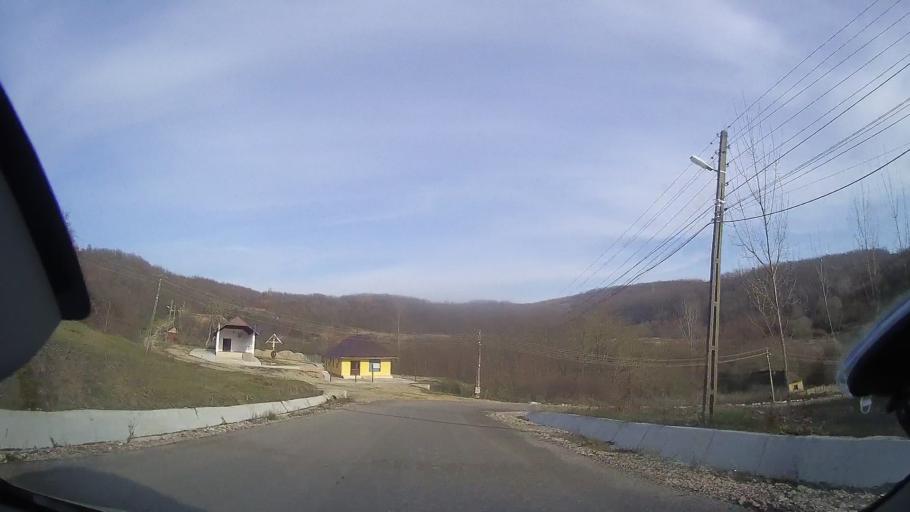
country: RO
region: Bihor
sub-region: Comuna Sarbi
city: Burzuc
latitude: 47.1767
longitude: 22.1512
